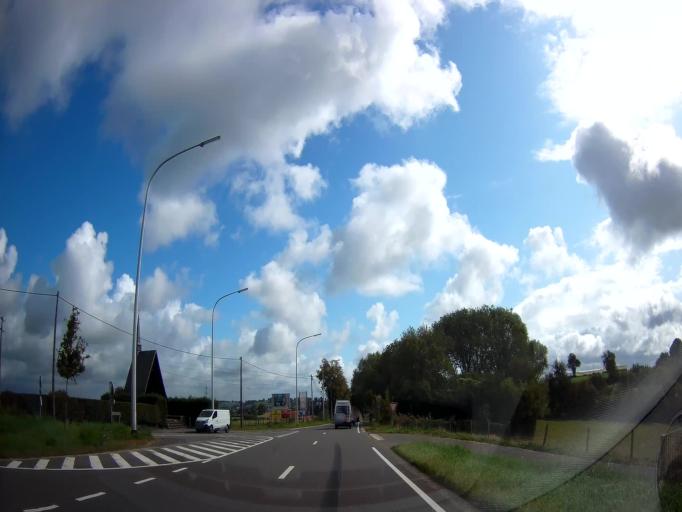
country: BE
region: Wallonia
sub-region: Province de Liege
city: Dison
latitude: 50.6452
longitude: 5.8474
